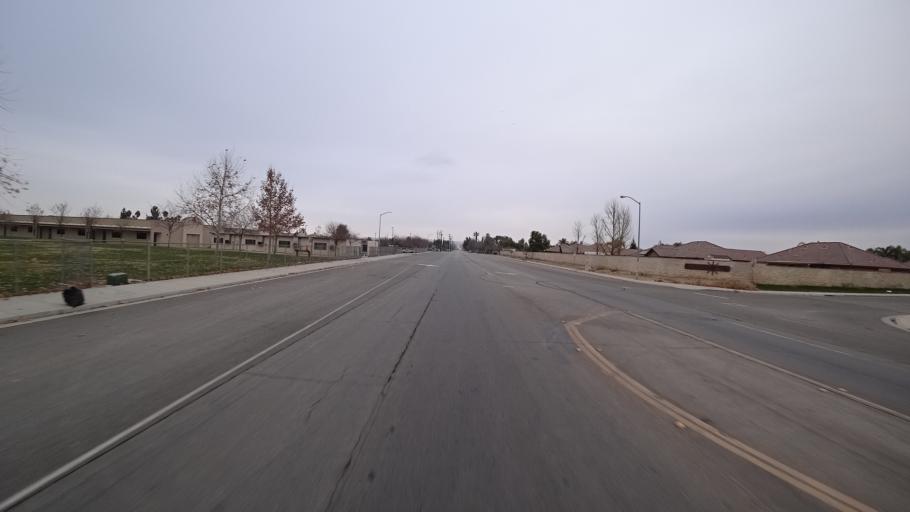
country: US
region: California
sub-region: Kern County
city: Lamont
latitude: 35.3453
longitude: -118.9320
